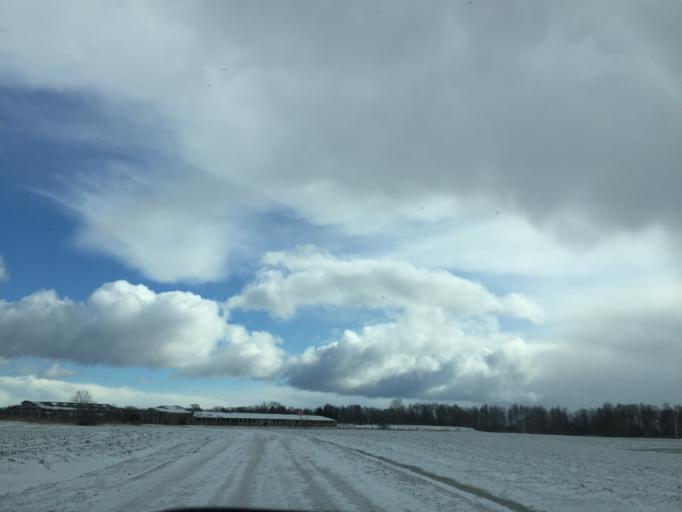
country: LV
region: Ventspils
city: Ventspils
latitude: 57.3716
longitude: 21.6271
